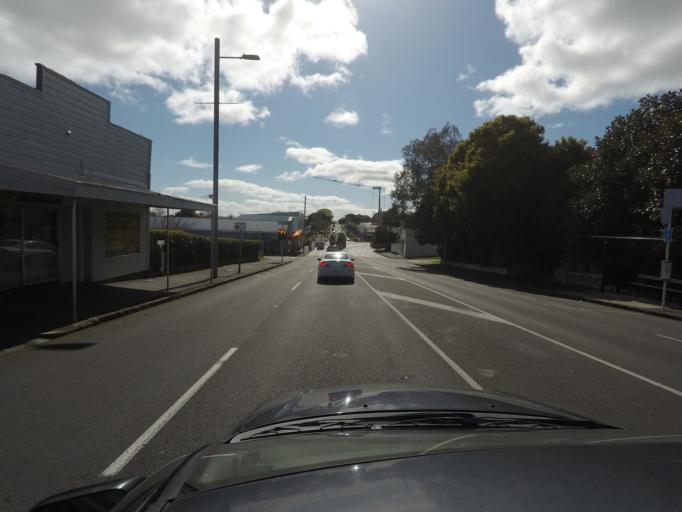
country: NZ
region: Auckland
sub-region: Auckland
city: Rosebank
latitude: -36.8831
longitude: 174.7169
